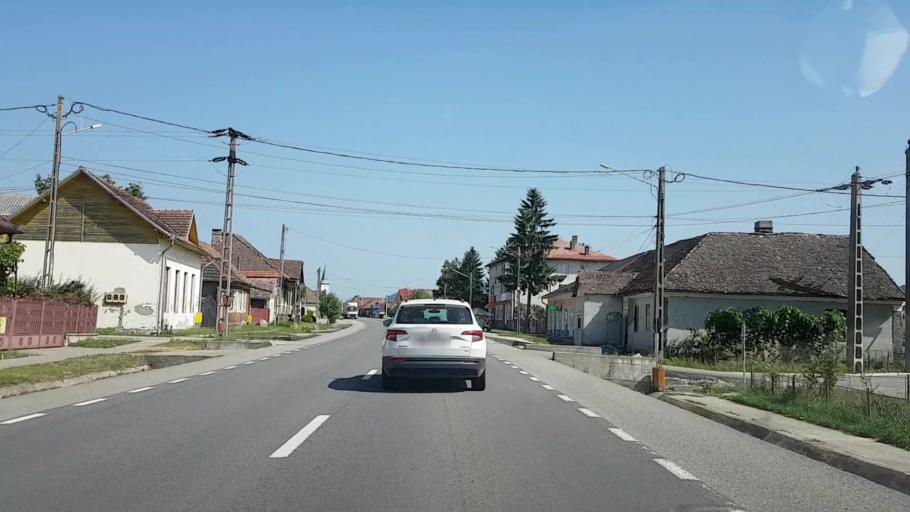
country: RO
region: Bistrita-Nasaud
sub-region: Comuna Sieu-Magherus
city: Sieu-Magherus
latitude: 47.0916
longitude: 24.3723
